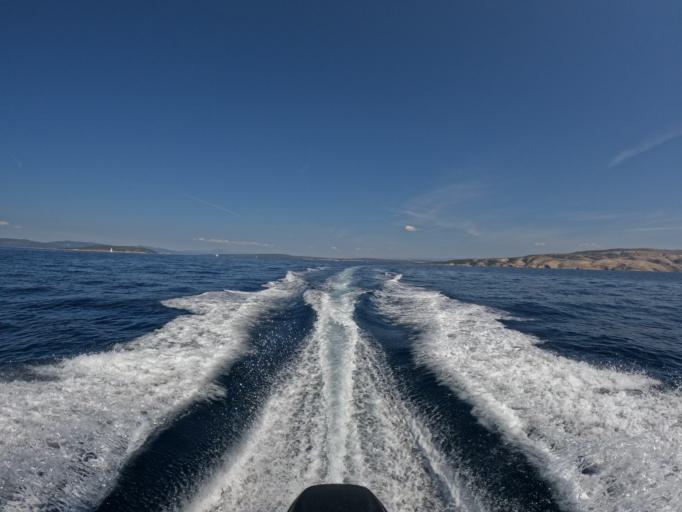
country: HR
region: Primorsko-Goranska
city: Punat
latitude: 44.9315
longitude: 14.6169
